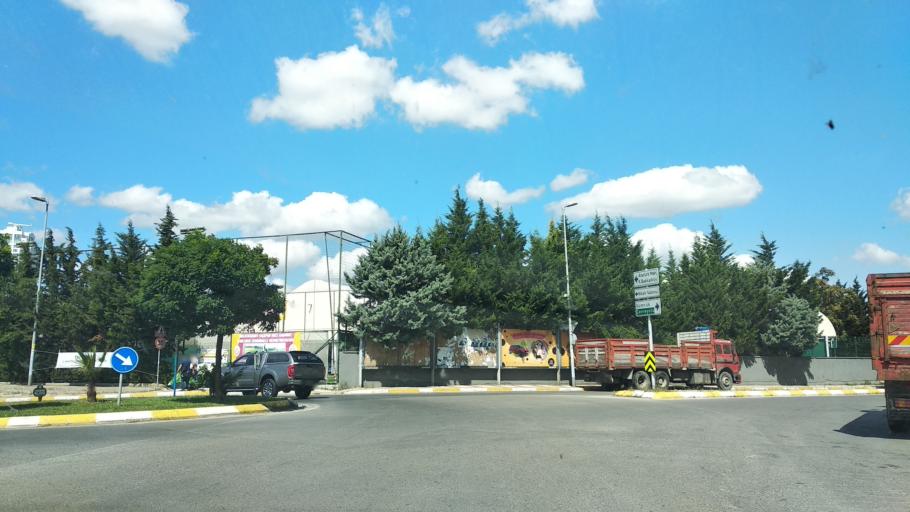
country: TR
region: Istanbul
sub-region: Atasehir
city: Atasehir
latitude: 40.9841
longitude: 29.1291
